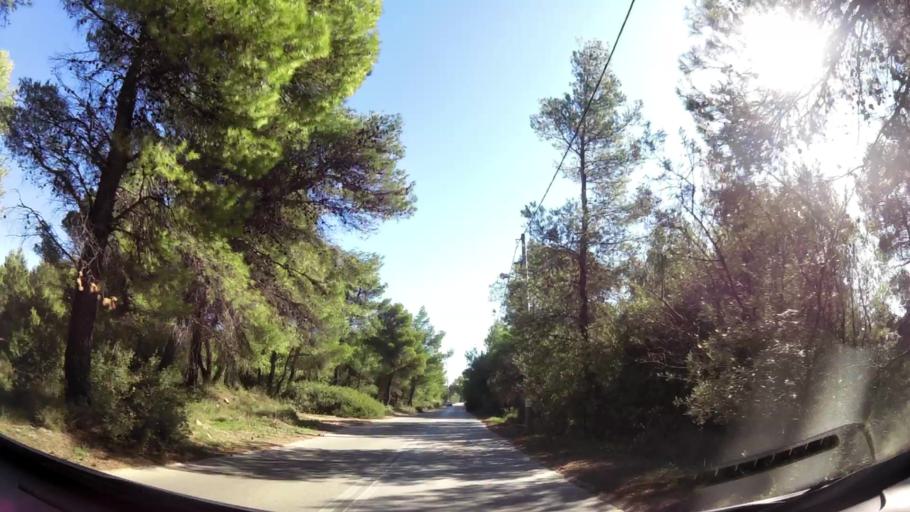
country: GR
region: Attica
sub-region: Nomarchia Anatolikis Attikis
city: Varybobi
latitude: 38.1333
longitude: 23.7818
